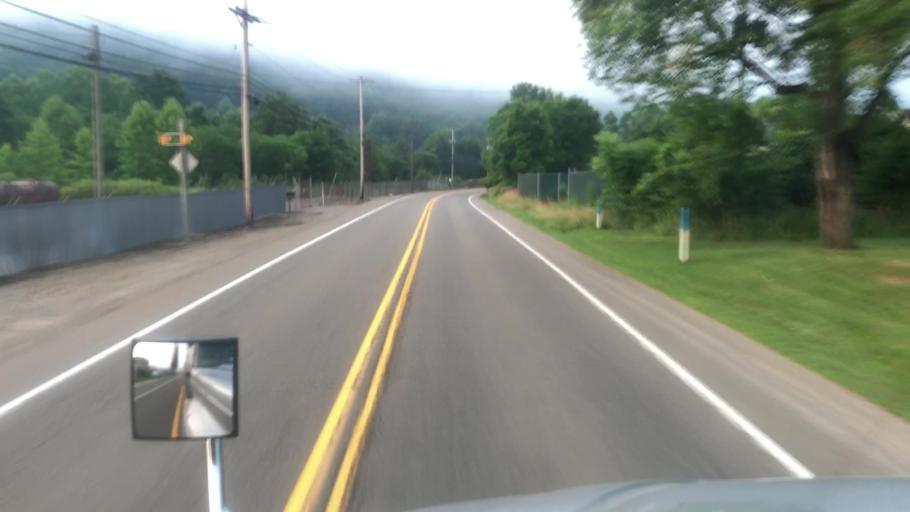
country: US
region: Pennsylvania
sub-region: Venango County
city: Hasson Heights
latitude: 41.4521
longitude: -79.6896
